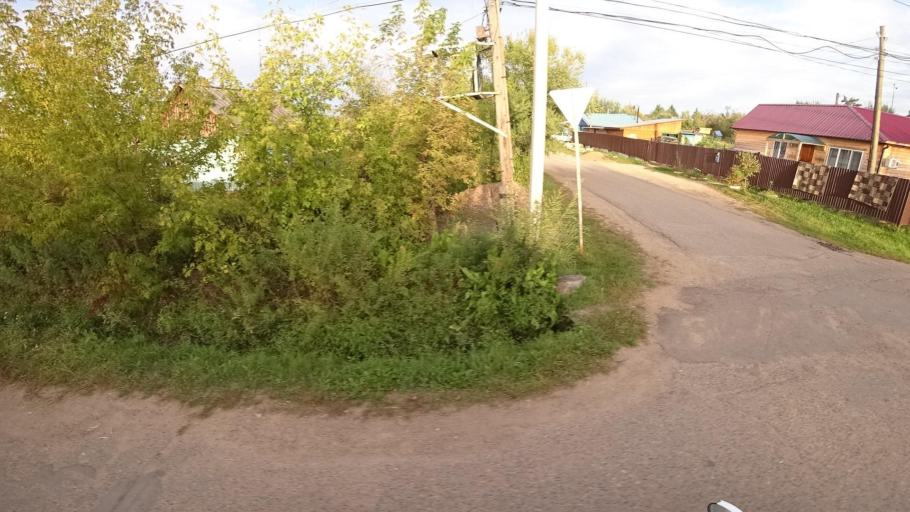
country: RU
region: Primorskiy
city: Yakovlevka
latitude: 44.4290
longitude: 133.4753
